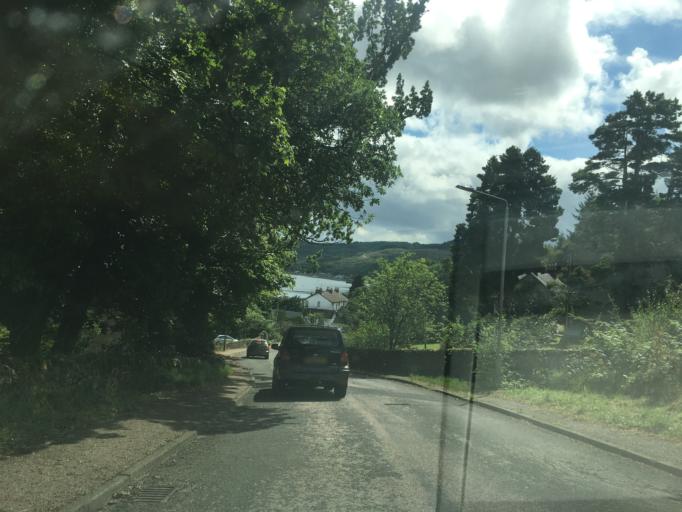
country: GB
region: Scotland
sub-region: Argyll and Bute
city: Tarbert
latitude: 55.9039
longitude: -5.2411
